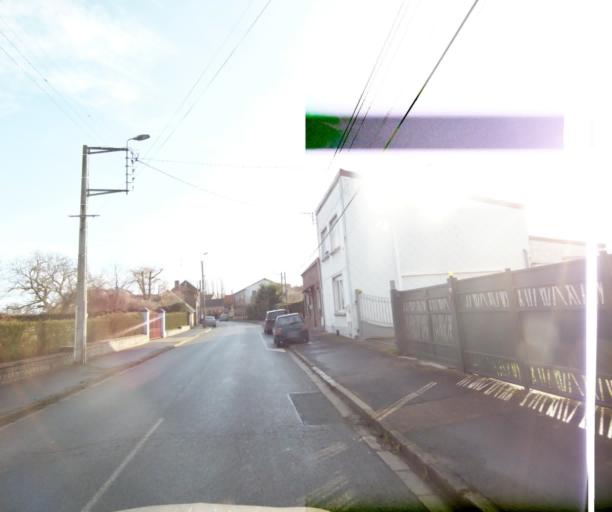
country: FR
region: Nord-Pas-de-Calais
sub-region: Departement du Nord
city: Maing
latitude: 50.3044
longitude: 3.4765
